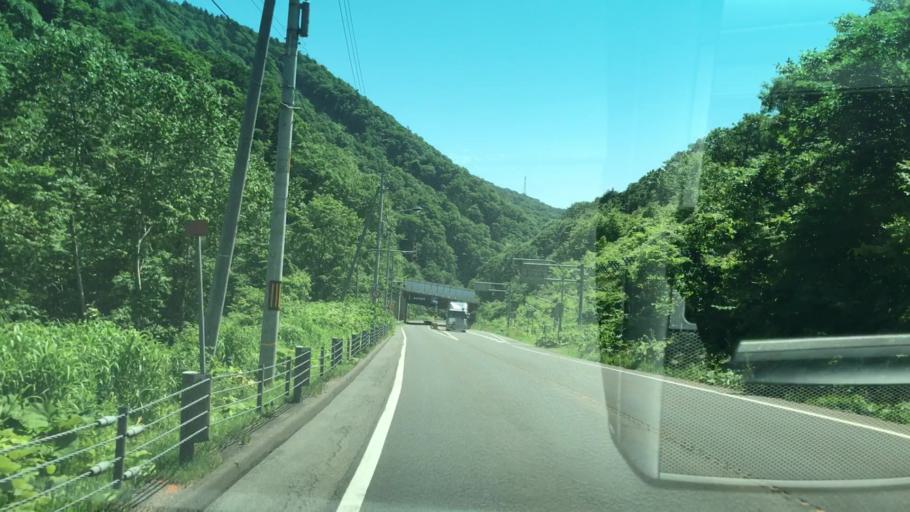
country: JP
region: Hokkaido
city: Yoichi
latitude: 43.0477
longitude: 140.6808
